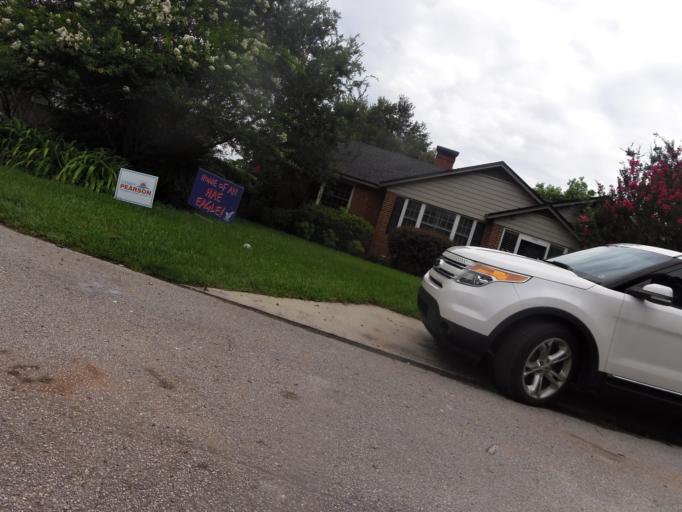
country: US
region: Florida
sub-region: Duval County
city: Jacksonville
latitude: 30.2772
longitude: -81.6536
